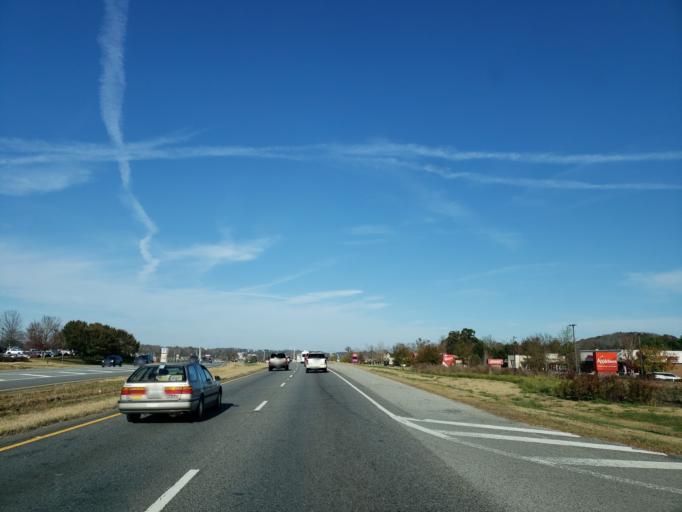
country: US
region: Georgia
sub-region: Dawson County
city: Dawsonville
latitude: 34.3464
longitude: -84.0495
